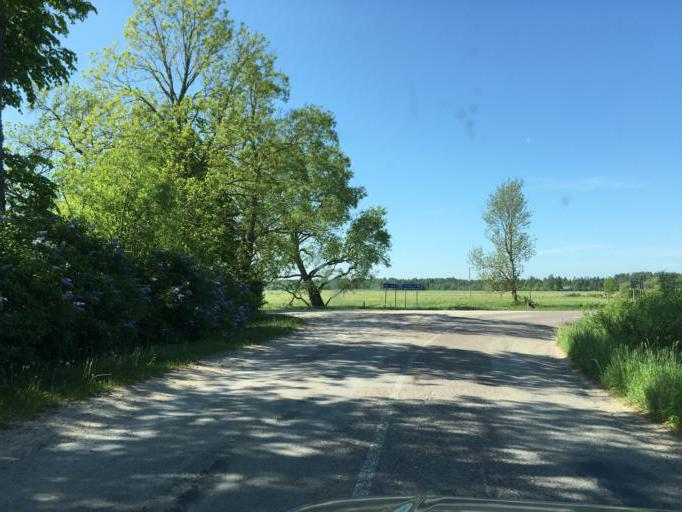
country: LV
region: Ventspils
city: Ventspils
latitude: 57.4997
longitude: 21.8421
